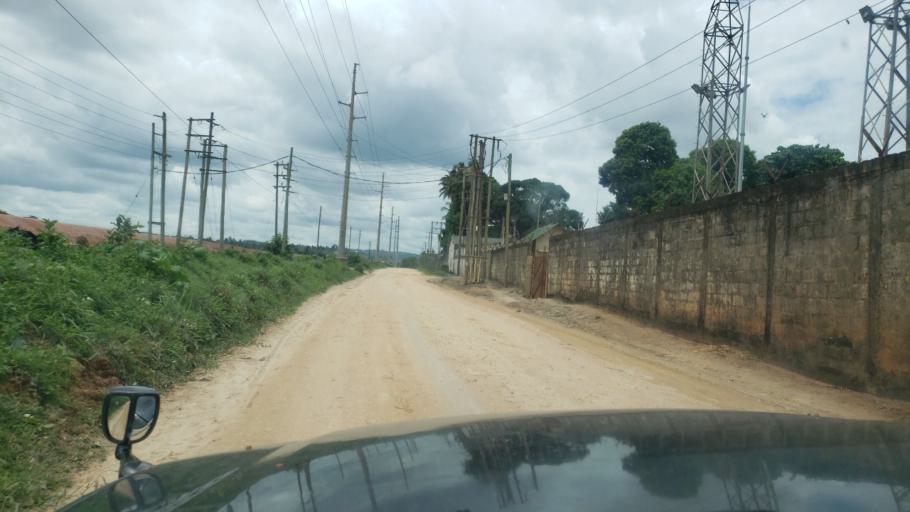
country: TZ
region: Pwani
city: Kisarawe
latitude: -6.8836
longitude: 39.1503
